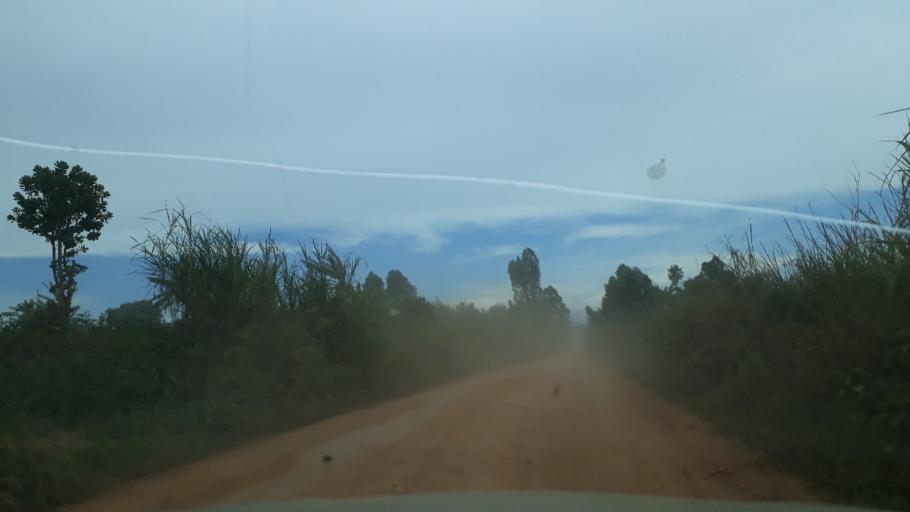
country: CD
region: Eastern Province
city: Bunia
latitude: 1.8999
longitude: 30.4995
